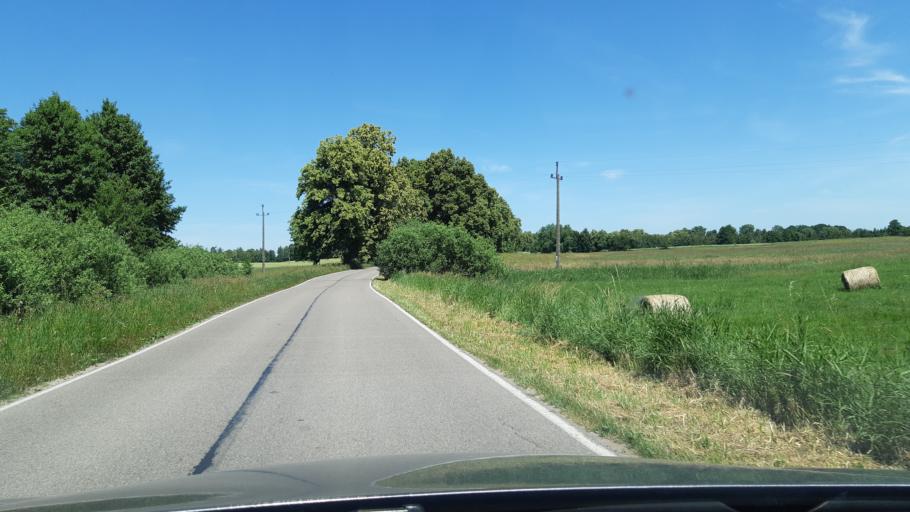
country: PL
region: Warmian-Masurian Voivodeship
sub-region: Powiat gizycki
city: Ryn
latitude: 53.9093
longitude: 21.6748
